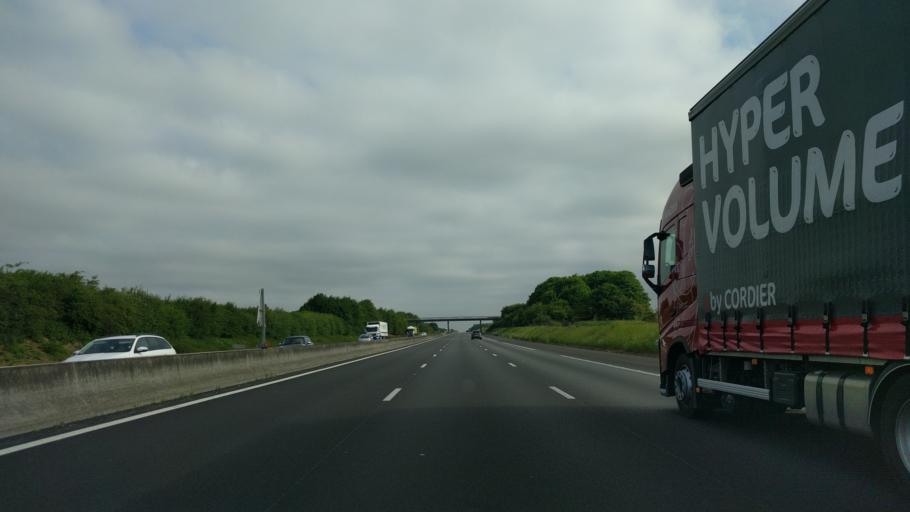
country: FR
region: Nord-Pas-de-Calais
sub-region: Departement du Pas-de-Calais
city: Bapaume
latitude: 50.1344
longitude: 2.8719
